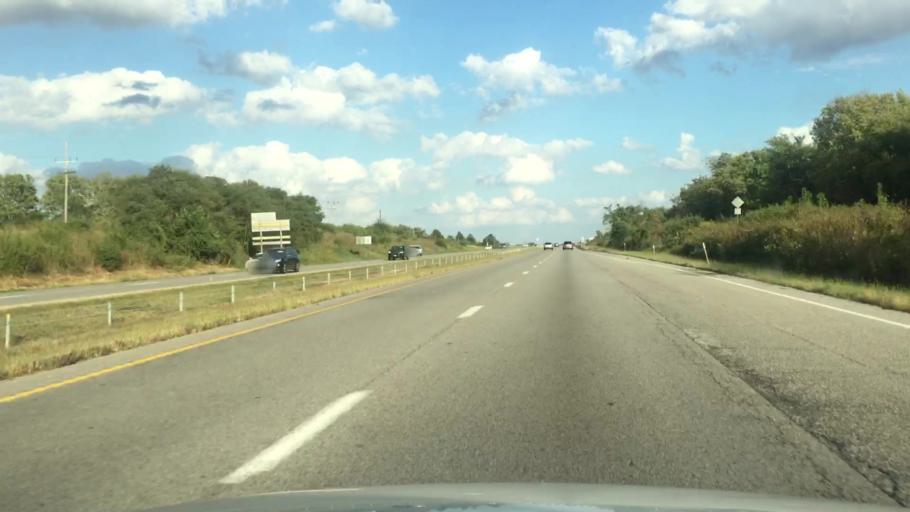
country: US
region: Missouri
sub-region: Lafayette County
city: Higginsville
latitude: 39.0024
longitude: -93.8056
